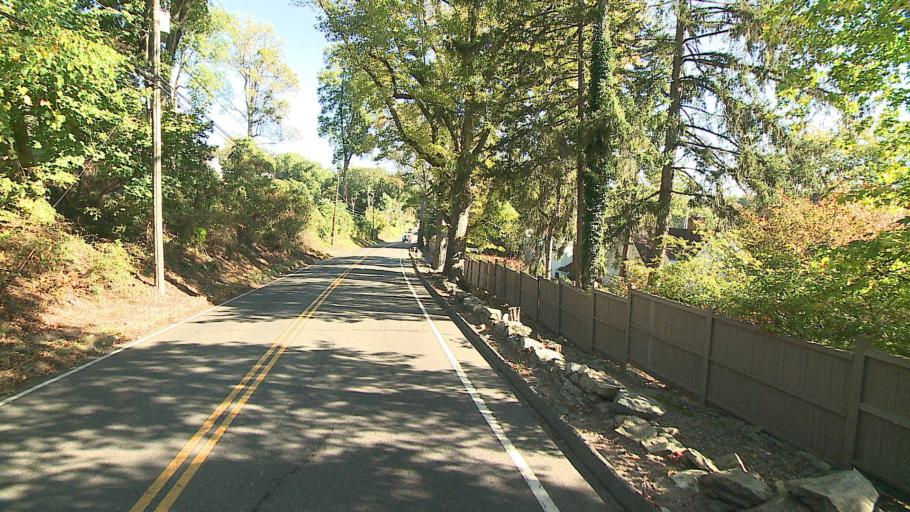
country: US
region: Connecticut
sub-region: Fairfield County
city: Darien
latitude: 41.0688
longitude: -73.4330
